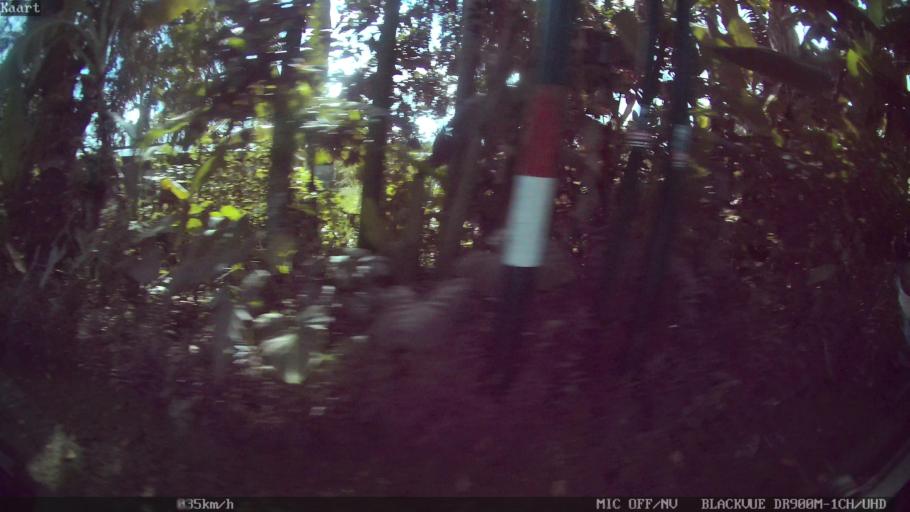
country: ID
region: Bali
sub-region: Kabupaten Gianyar
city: Ubud
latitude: -8.5211
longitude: 115.3004
